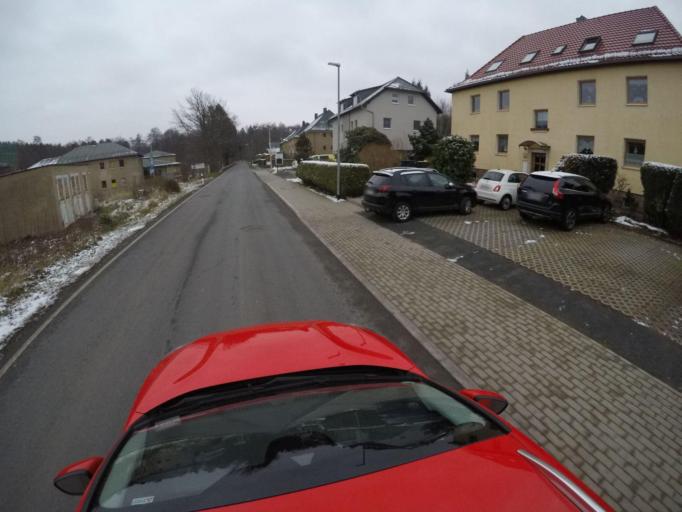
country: DE
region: Saxony
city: Dohma
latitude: 50.8770
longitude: 13.9591
